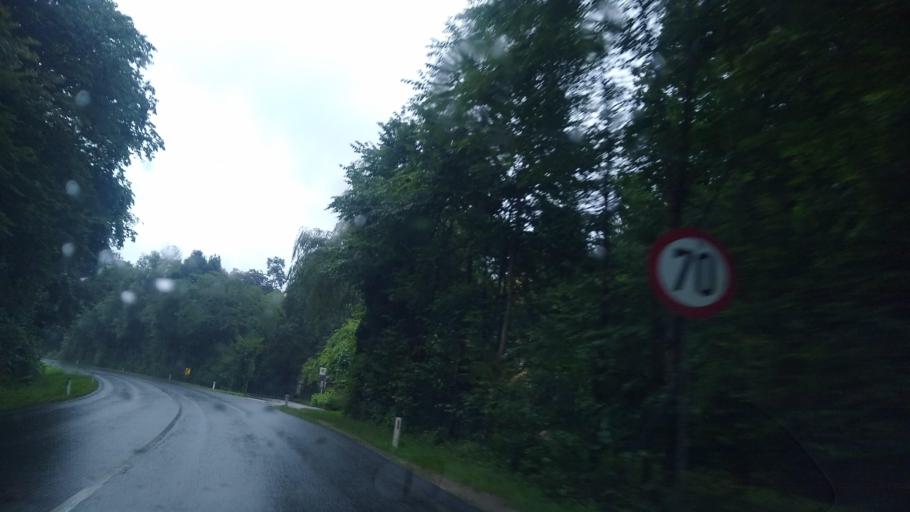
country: AT
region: Tyrol
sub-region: Politischer Bezirk Kufstein
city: Reith im Alpbachtal
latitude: 47.4185
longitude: 11.8621
